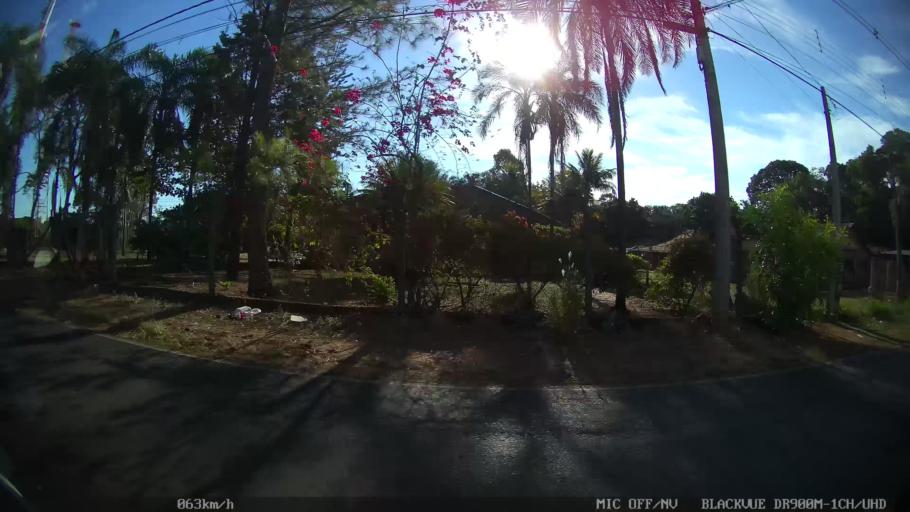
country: BR
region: Sao Paulo
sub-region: Araraquara
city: Araraquara
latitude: -21.7637
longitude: -48.1438
